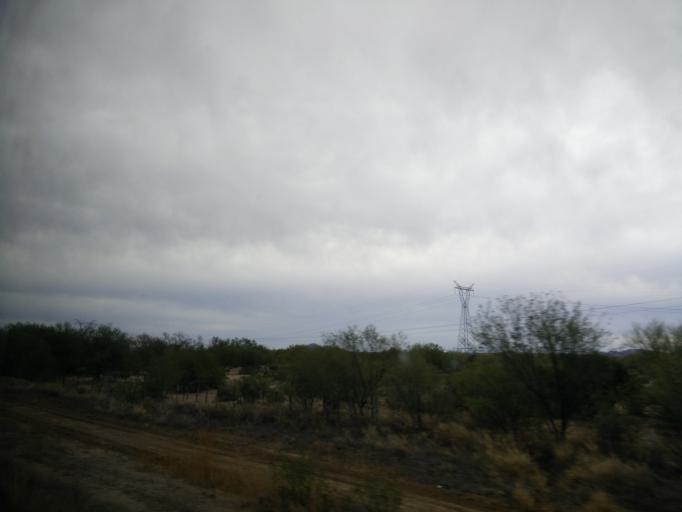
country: MX
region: Sonora
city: Hermosillo
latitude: 28.6853
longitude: -110.9912
